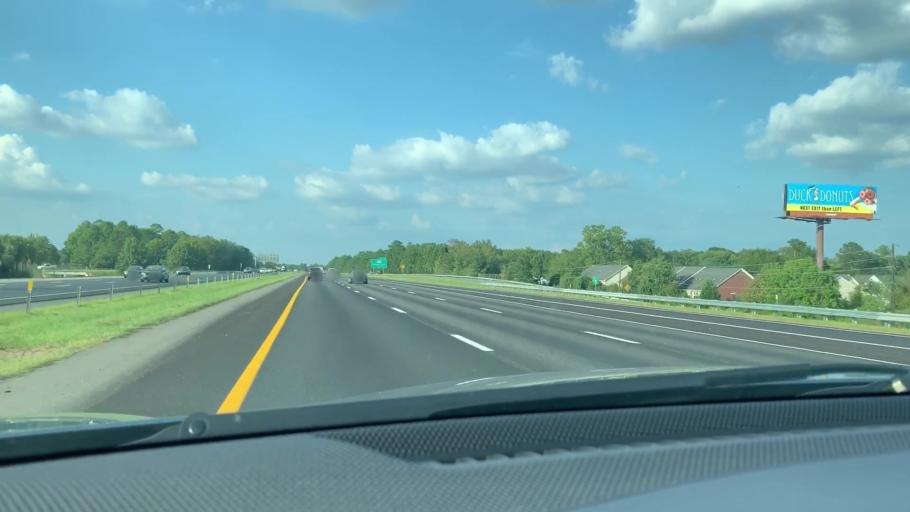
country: US
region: South Carolina
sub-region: Richland County
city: Forest Acres
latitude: 33.9772
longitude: -80.9548
